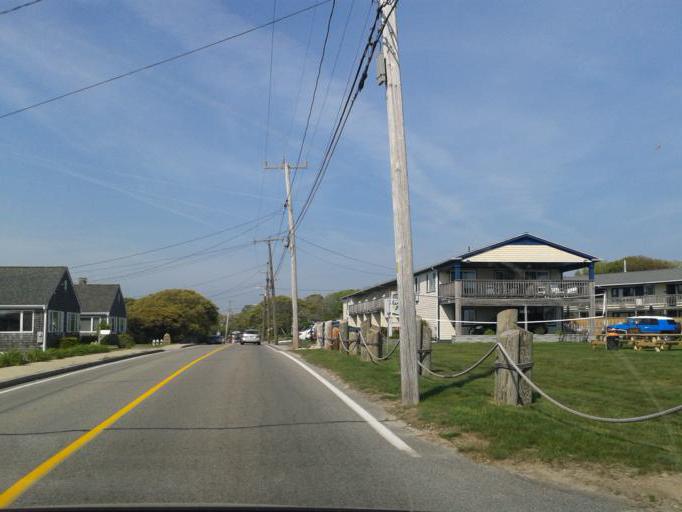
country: US
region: Massachusetts
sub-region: Barnstable County
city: Falmouth
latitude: 41.5436
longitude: -70.6041
